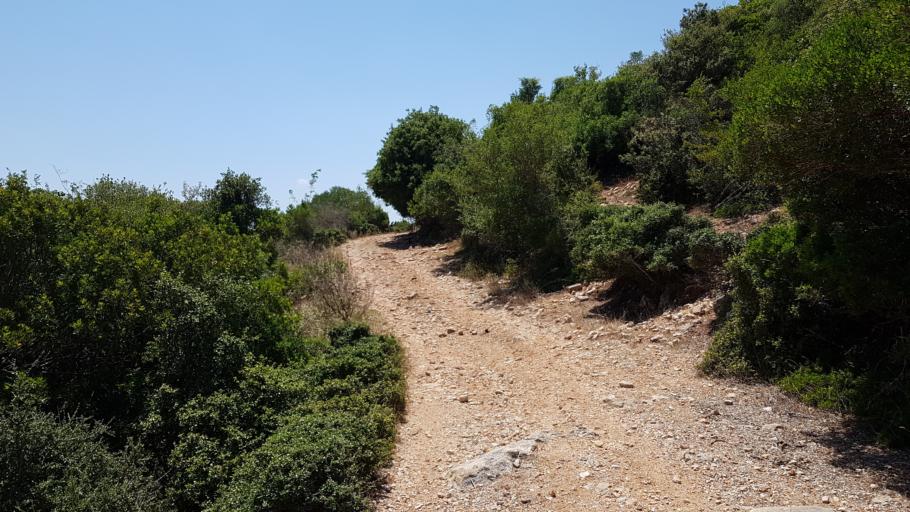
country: AL
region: Vlore
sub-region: Rrethi i Sarandes
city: Xarre
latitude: 39.7512
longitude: 19.9957
